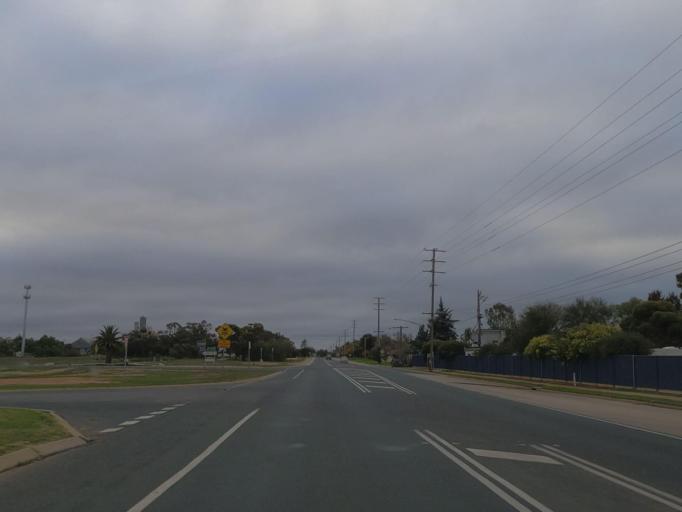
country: AU
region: Victoria
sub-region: Swan Hill
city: Swan Hill
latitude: -35.4624
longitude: 143.6349
